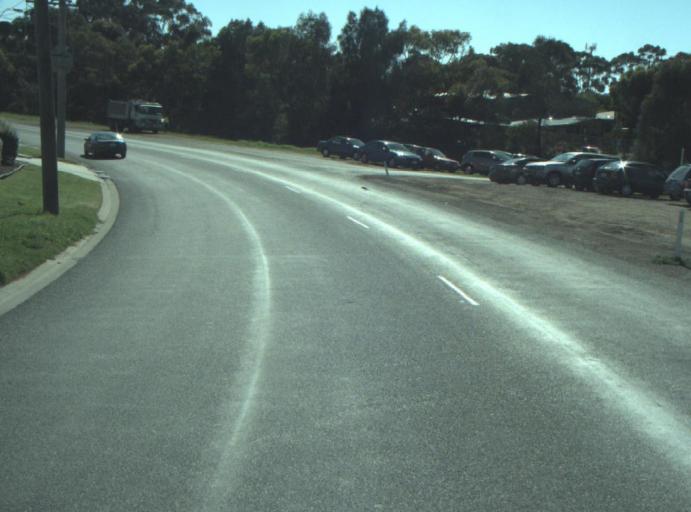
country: AU
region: Victoria
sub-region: Greater Geelong
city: Bell Park
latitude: -38.1001
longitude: 144.3484
